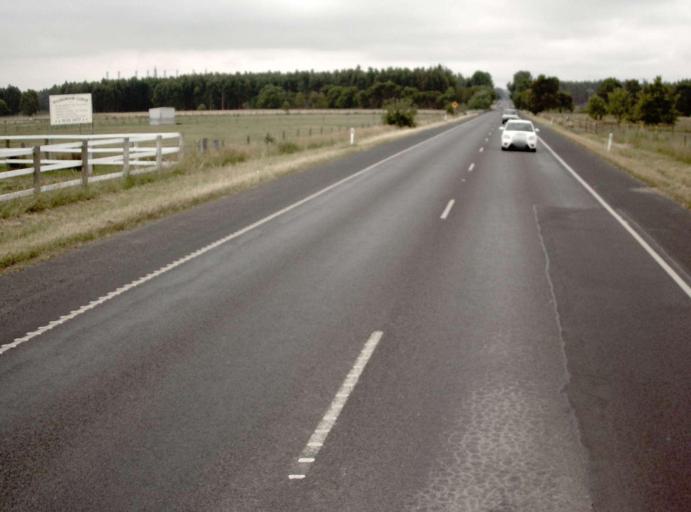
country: AU
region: Victoria
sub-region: Latrobe
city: Morwell
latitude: -38.2967
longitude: 146.4172
